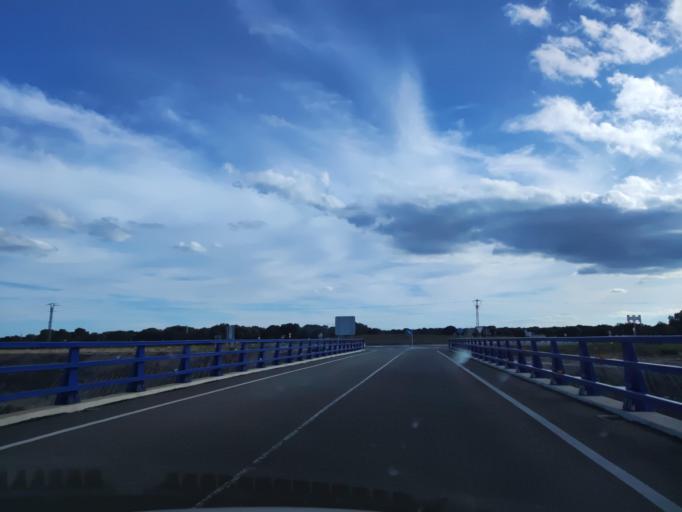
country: ES
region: Castille and Leon
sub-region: Provincia de Salamanca
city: Fuentes de Onoro
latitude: 40.5940
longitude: -6.7969
